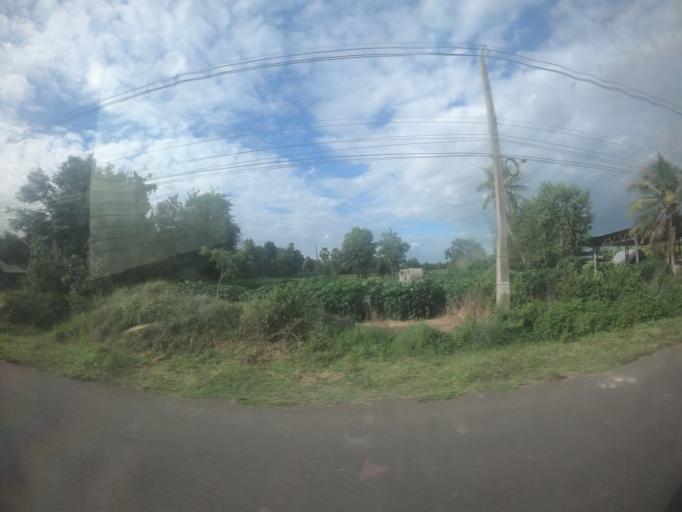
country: TH
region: Surin
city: Prasat
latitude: 14.6054
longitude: 103.4262
